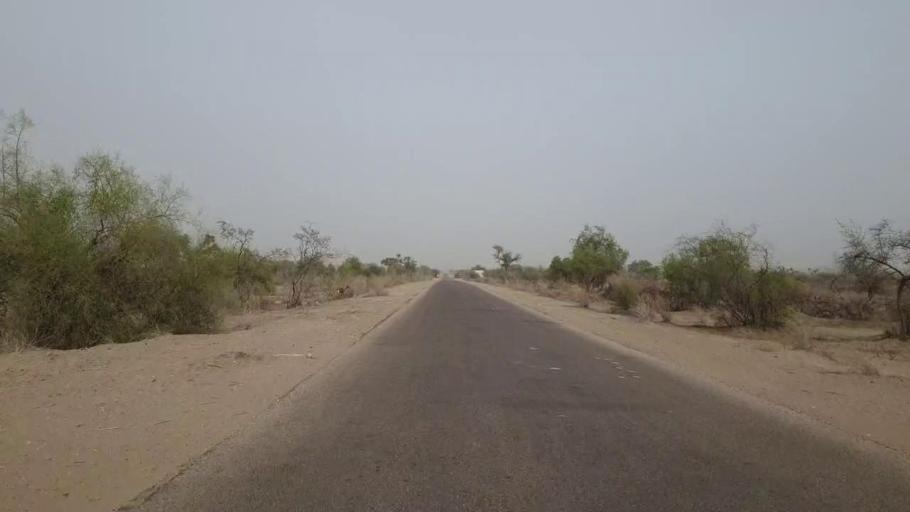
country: PK
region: Sindh
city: Islamkot
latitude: 24.5755
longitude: 70.3128
